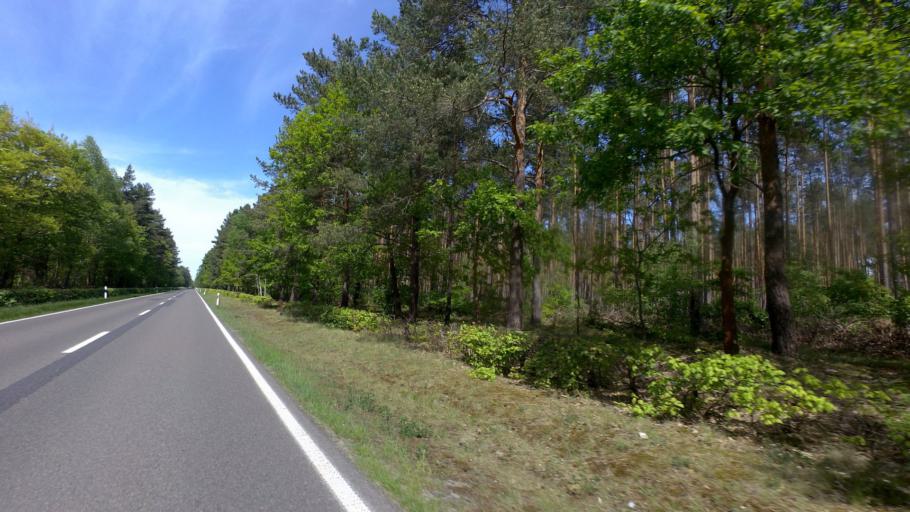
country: DE
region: Brandenburg
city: Sperenberg
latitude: 52.1117
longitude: 13.3710
